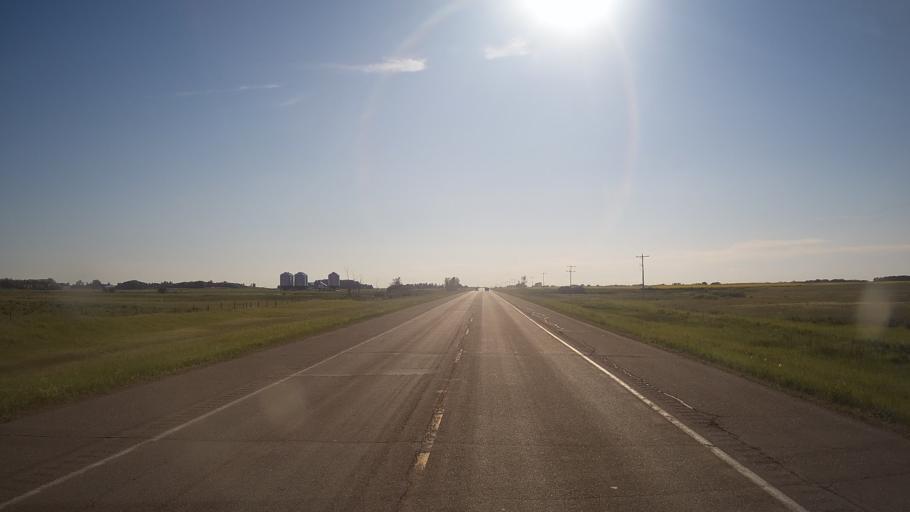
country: CA
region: Saskatchewan
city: Lanigan
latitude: 51.7944
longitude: -104.6921
